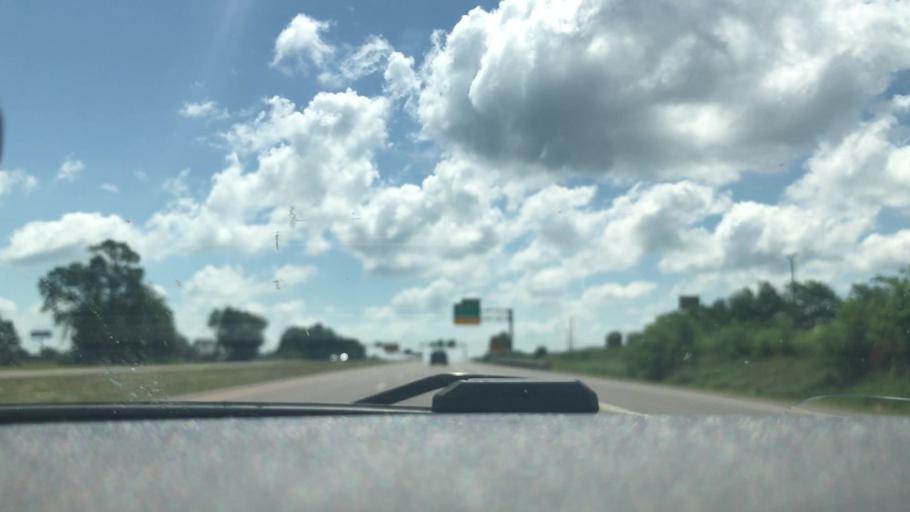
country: US
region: Wisconsin
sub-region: Eau Claire County
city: Altoona
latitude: 44.7758
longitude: -91.4333
